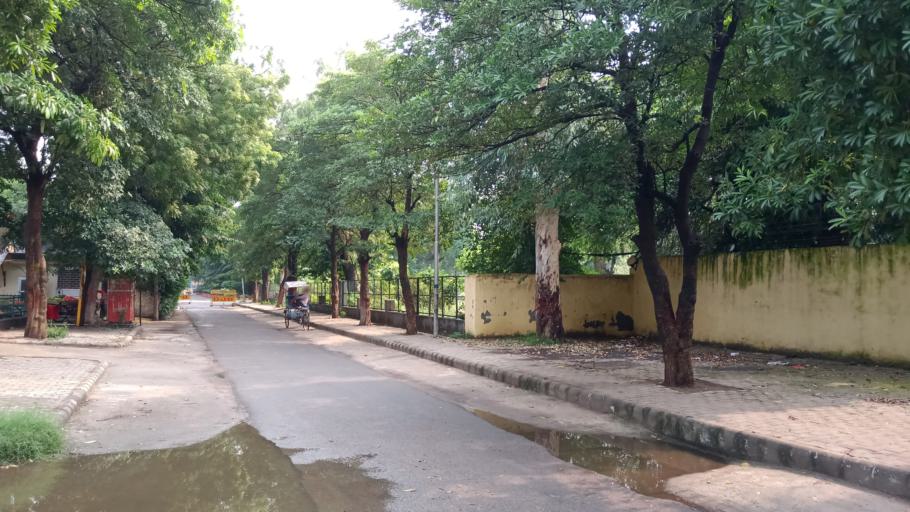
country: IN
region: NCT
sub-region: New Delhi
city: New Delhi
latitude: 28.5770
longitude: 77.2474
